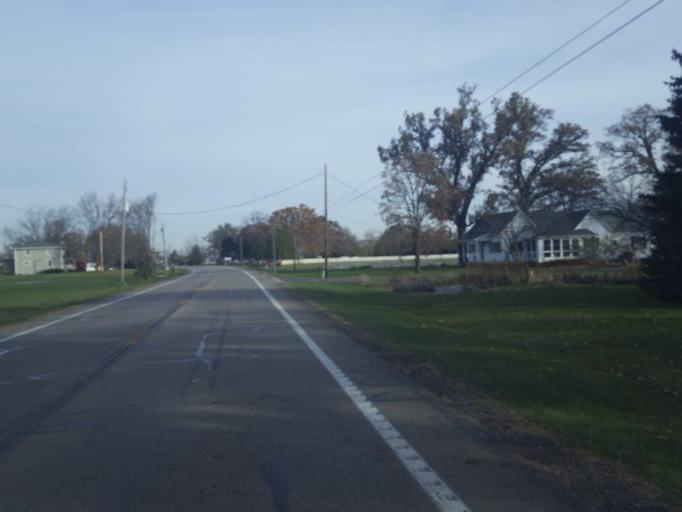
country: US
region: Ohio
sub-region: Madison County
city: Plain City
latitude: 40.0974
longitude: -83.2798
